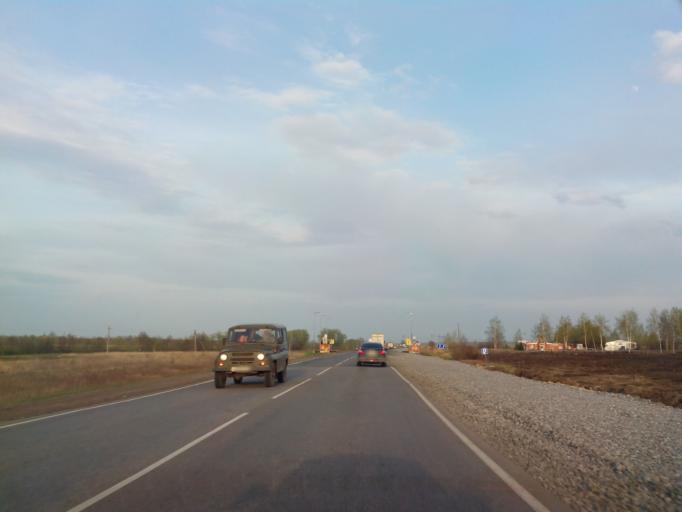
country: RU
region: Rjazan
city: Korablino
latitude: 53.7515
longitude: 39.8432
